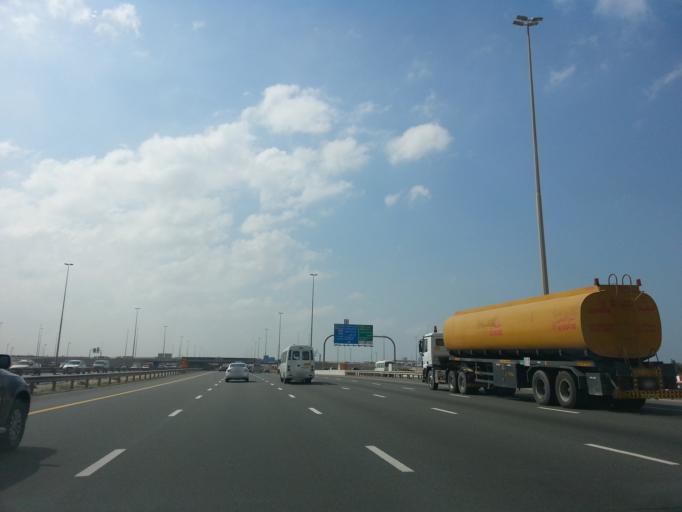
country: AE
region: Dubai
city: Dubai
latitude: 25.1727
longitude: 55.2710
